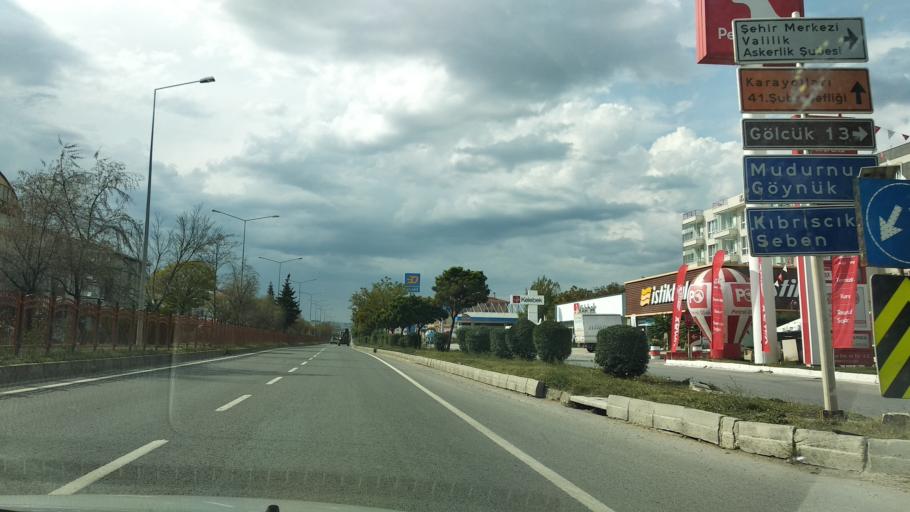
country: TR
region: Bolu
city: Bolu
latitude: 40.7374
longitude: 31.5978
